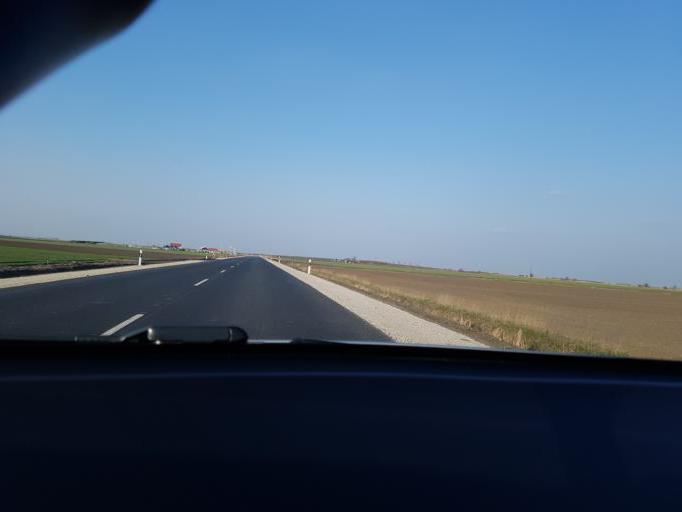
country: RO
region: Arad
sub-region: Comuna Nadlac
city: Nadlac
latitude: 46.1976
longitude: 20.7148
